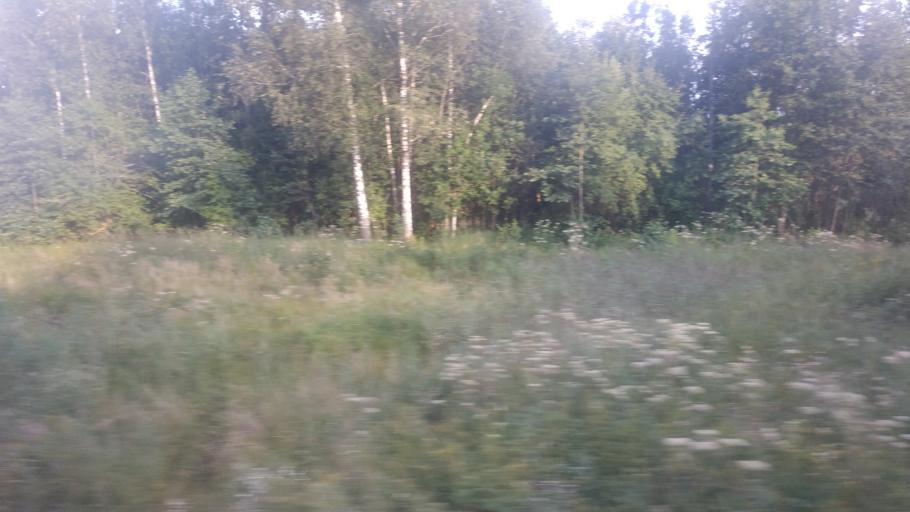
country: RU
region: Moskovskaya
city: Kerva
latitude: 55.5506
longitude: 39.6913
